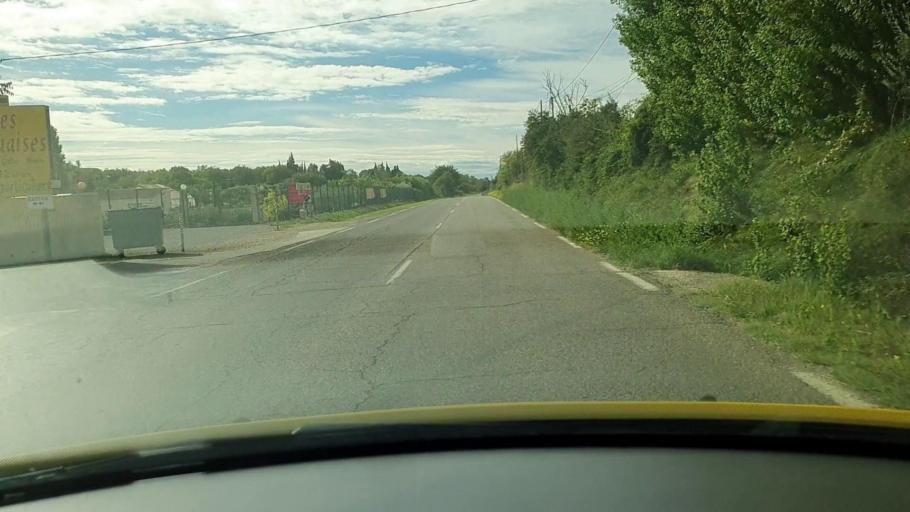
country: FR
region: Languedoc-Roussillon
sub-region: Departement du Gard
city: Saint-Gilles
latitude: 43.6959
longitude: 4.4487
